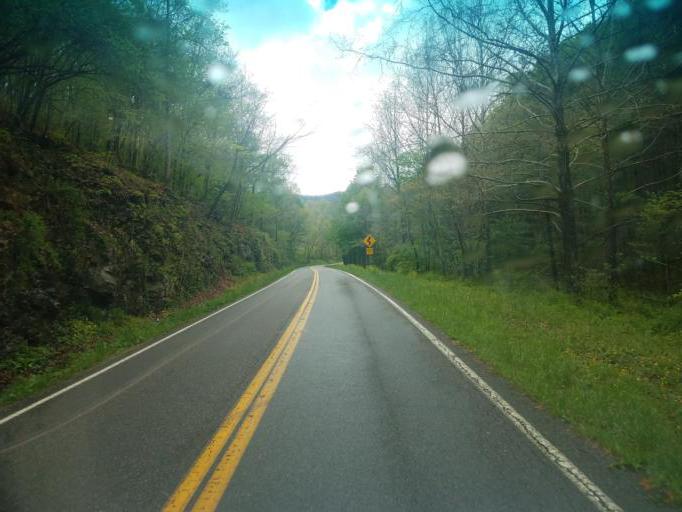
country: US
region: Virginia
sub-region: Smyth County
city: Marion
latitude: 36.9408
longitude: -81.5291
